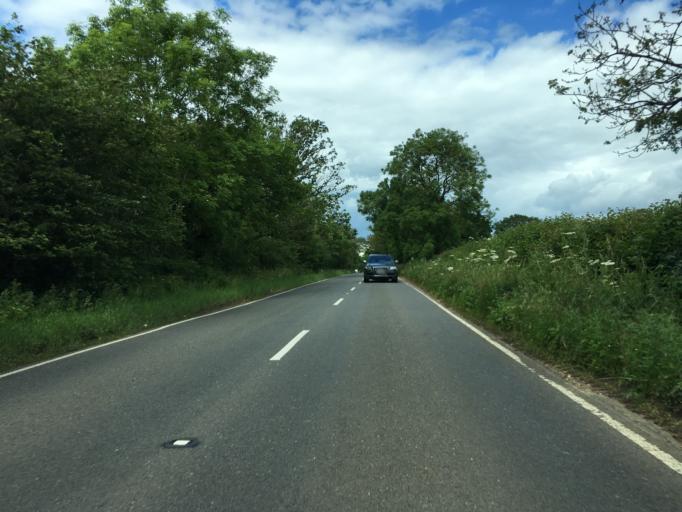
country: GB
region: England
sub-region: Northamptonshire
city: Brackley
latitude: 52.0713
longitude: -1.1080
